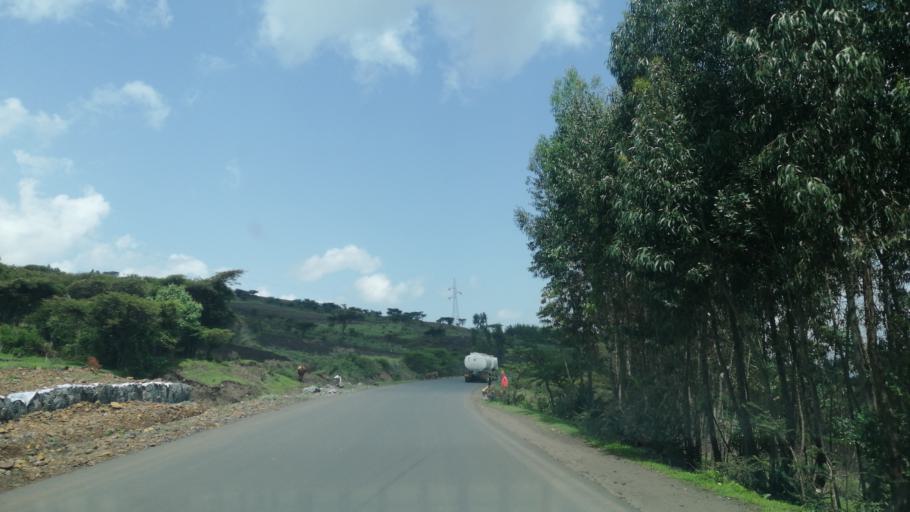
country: ET
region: Oromiya
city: Guder
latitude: 8.9944
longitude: 37.6207
